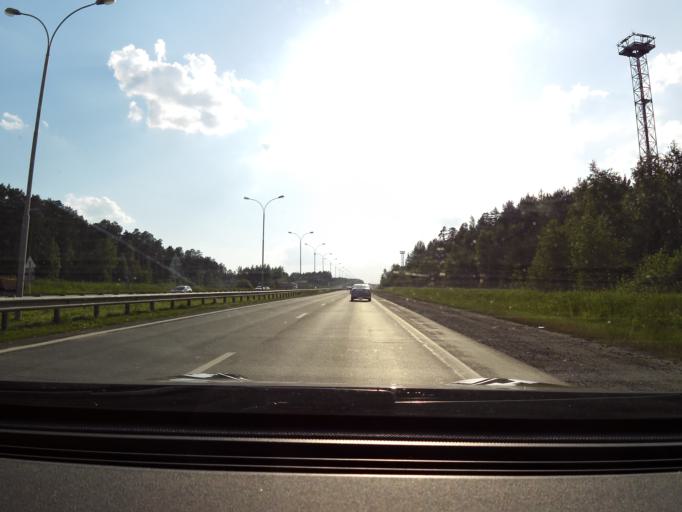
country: RU
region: Sverdlovsk
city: Shirokaya Rechka
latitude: 56.8258
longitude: 60.4903
